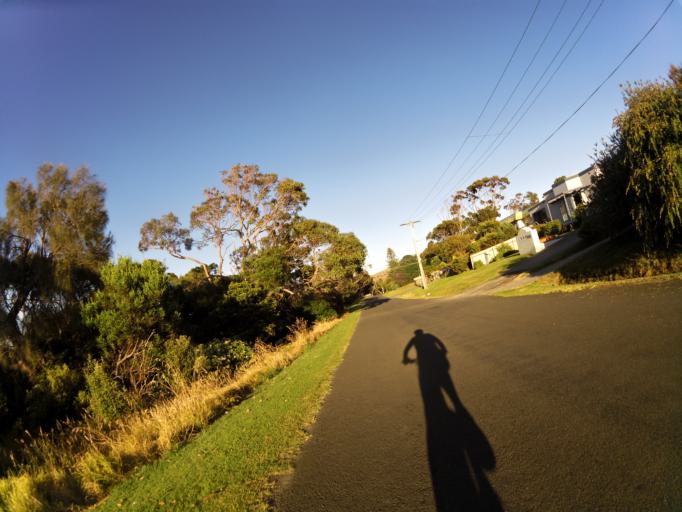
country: AU
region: Victoria
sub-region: Colac-Otway
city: Apollo Bay
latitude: -38.7614
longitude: 143.6674
